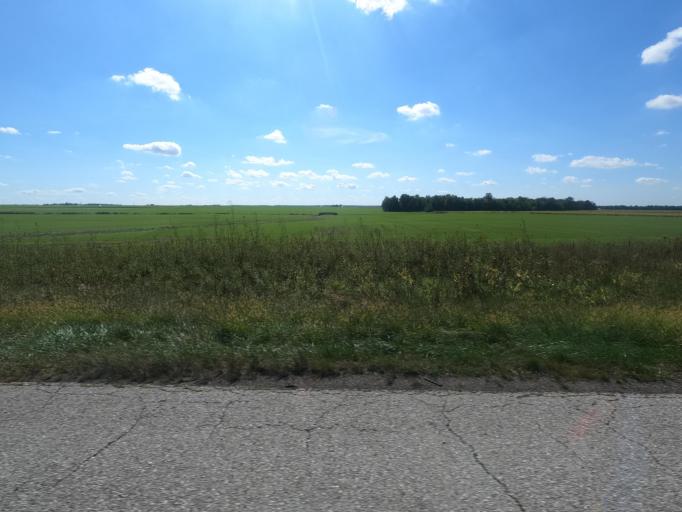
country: US
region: Illinois
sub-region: Washington County
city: Nashville
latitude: 38.3903
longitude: -89.2598
